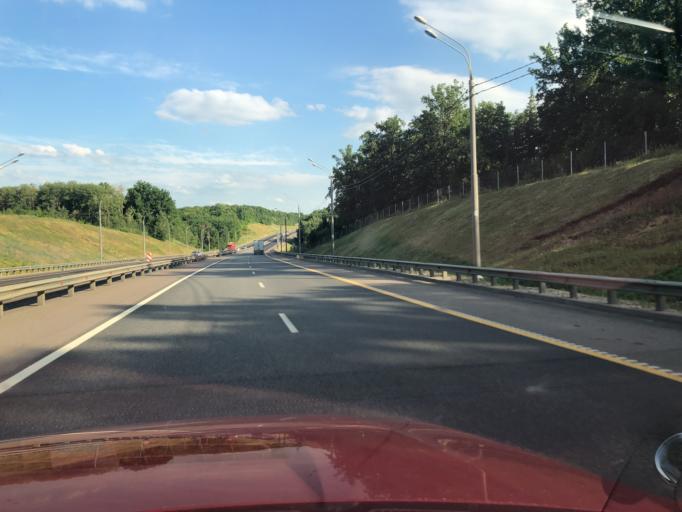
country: RU
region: Lipetsk
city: Zadonsk
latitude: 52.4073
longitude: 38.8532
